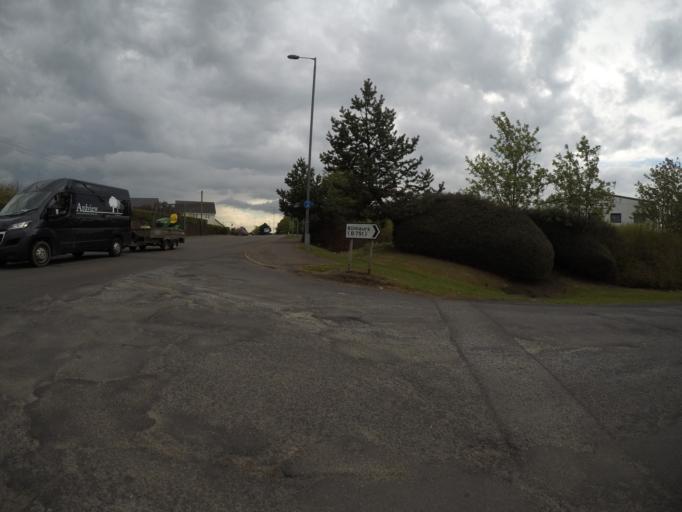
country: GB
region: Scotland
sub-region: East Ayrshire
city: Kilmarnock
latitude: 55.6392
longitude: -4.4737
